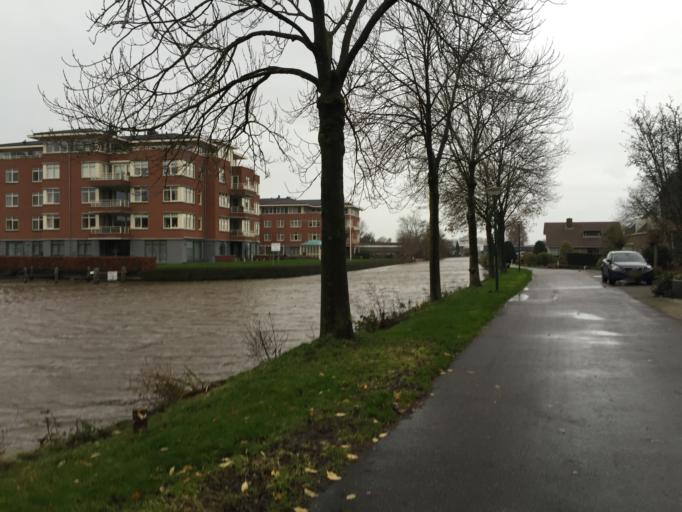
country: NL
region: Utrecht
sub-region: Gemeente Montfoort
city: Montfoort
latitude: 52.0450
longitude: 4.9447
